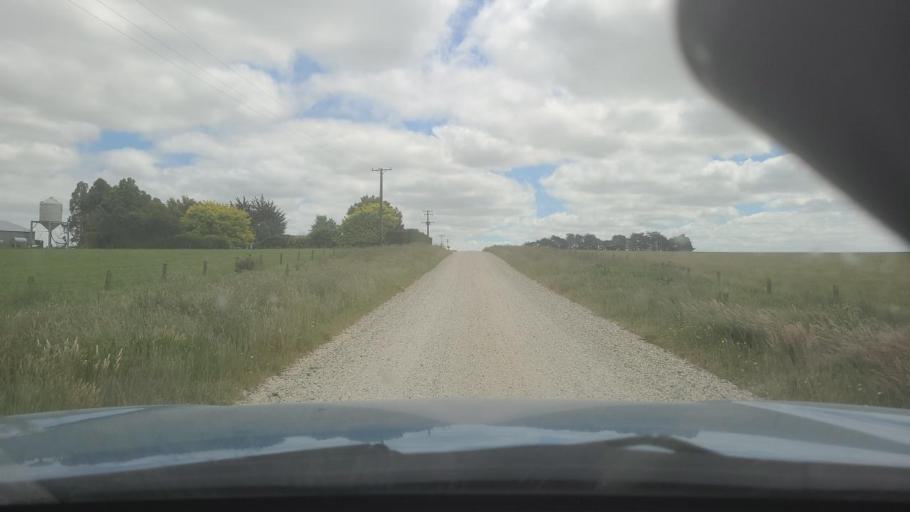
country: NZ
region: Southland
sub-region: Invercargill City
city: Invercargill
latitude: -46.3306
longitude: 168.5925
